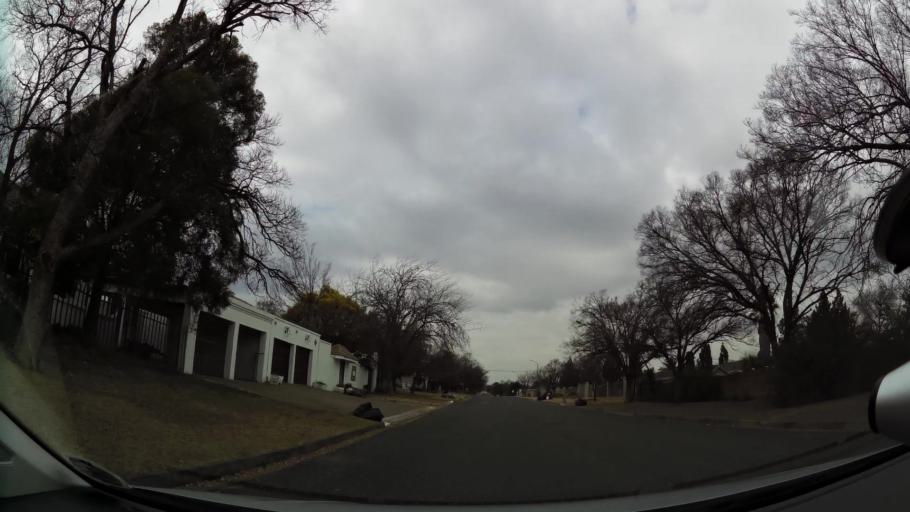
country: ZA
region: Orange Free State
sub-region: Fezile Dabi District Municipality
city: Kroonstad
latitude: -27.6771
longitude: 27.2434
